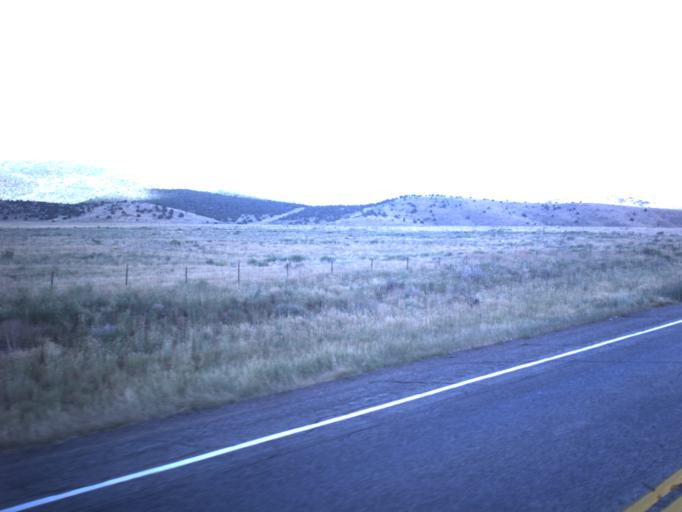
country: US
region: Utah
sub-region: Utah County
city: Woodland Hills
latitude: 39.8467
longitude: -111.5168
